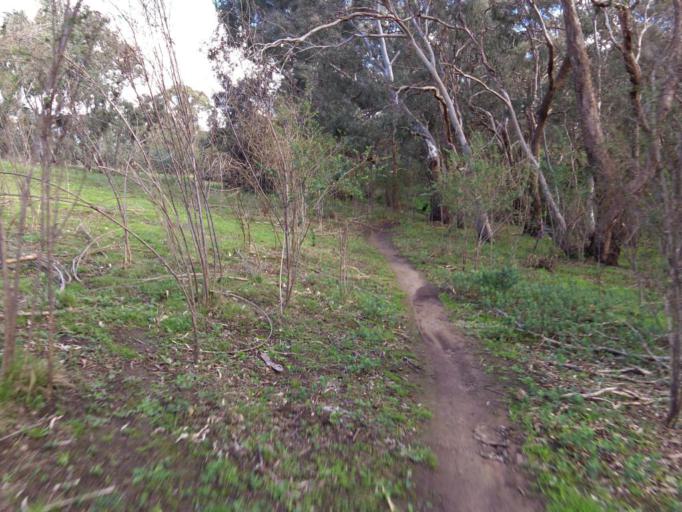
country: AU
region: Victoria
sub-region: Banyule
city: Watsonia North
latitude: -37.6839
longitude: 145.0797
